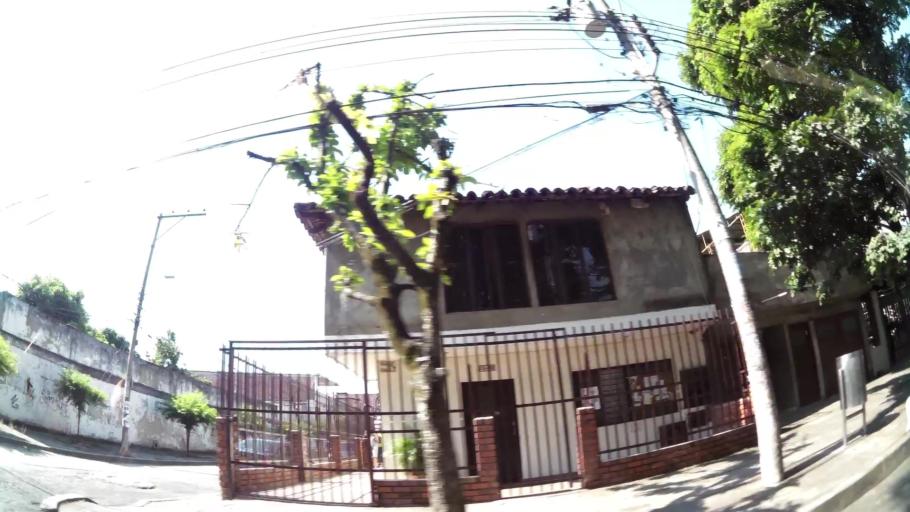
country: CO
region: Valle del Cauca
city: Cali
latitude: 3.4060
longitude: -76.5262
